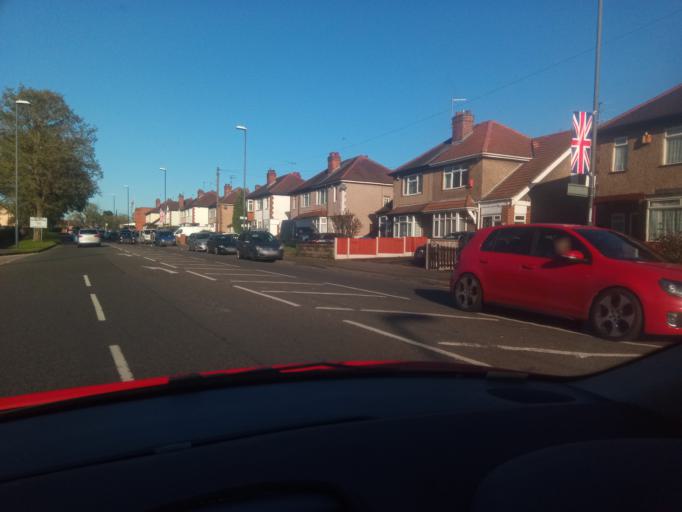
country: GB
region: England
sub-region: Derby
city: Derby
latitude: 52.8849
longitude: -1.4491
